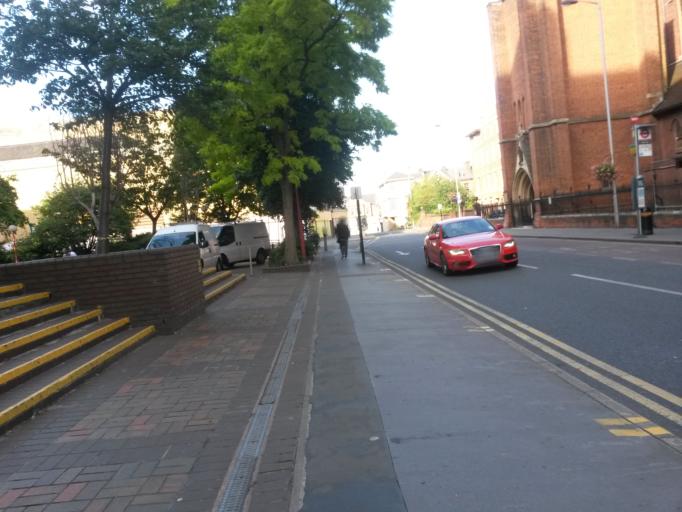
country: GB
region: England
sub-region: Greater London
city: Croydon
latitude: 51.3780
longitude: -0.1006
